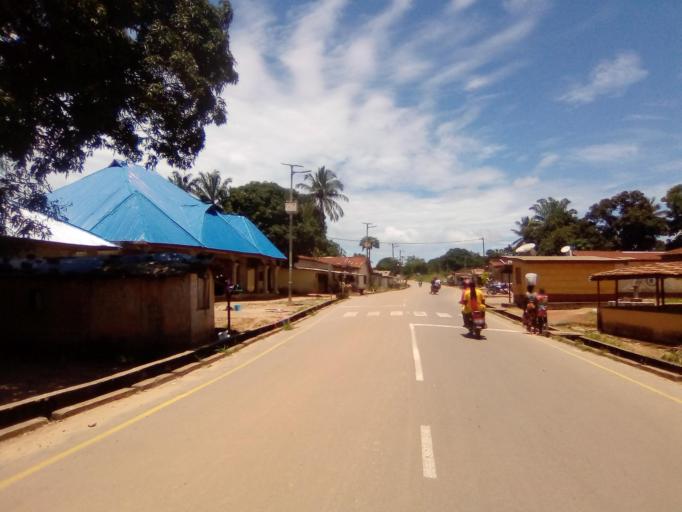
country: SL
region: Eastern Province
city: Koidu
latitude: 8.6400
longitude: -10.9670
